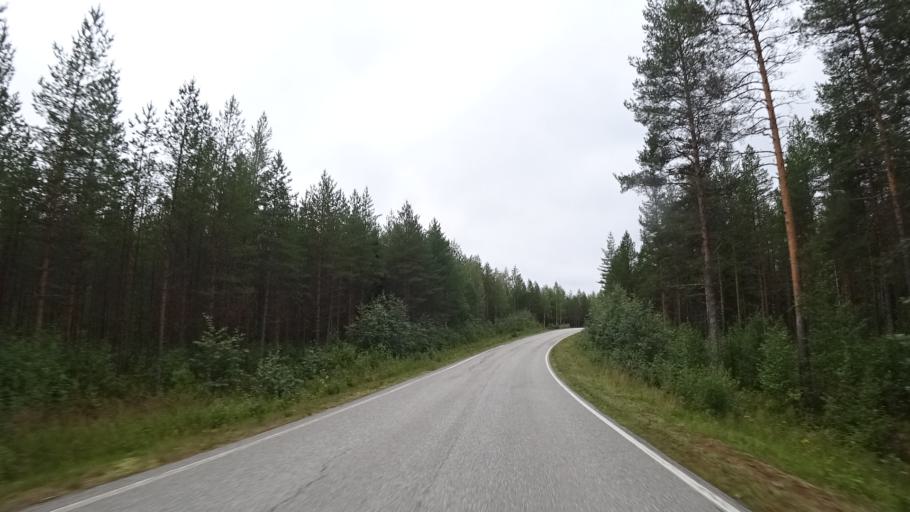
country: FI
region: North Karelia
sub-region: Pielisen Karjala
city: Lieksa
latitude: 63.3642
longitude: 30.2868
